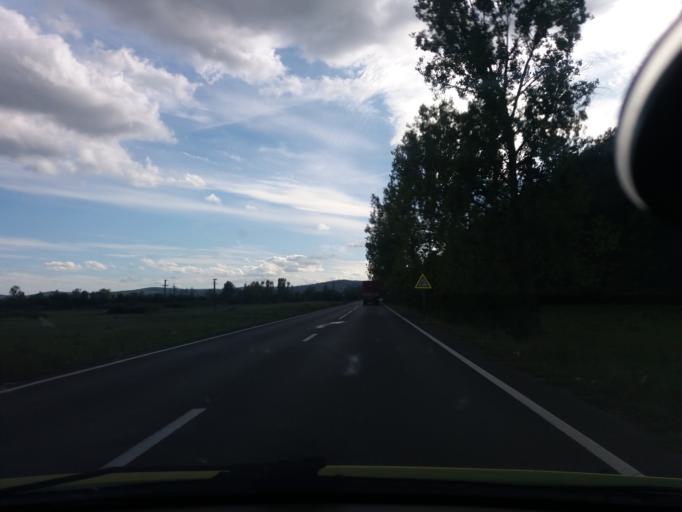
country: RO
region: Arad
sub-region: Comuna Ususau
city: Ususau
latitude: 46.0976
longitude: 21.8130
